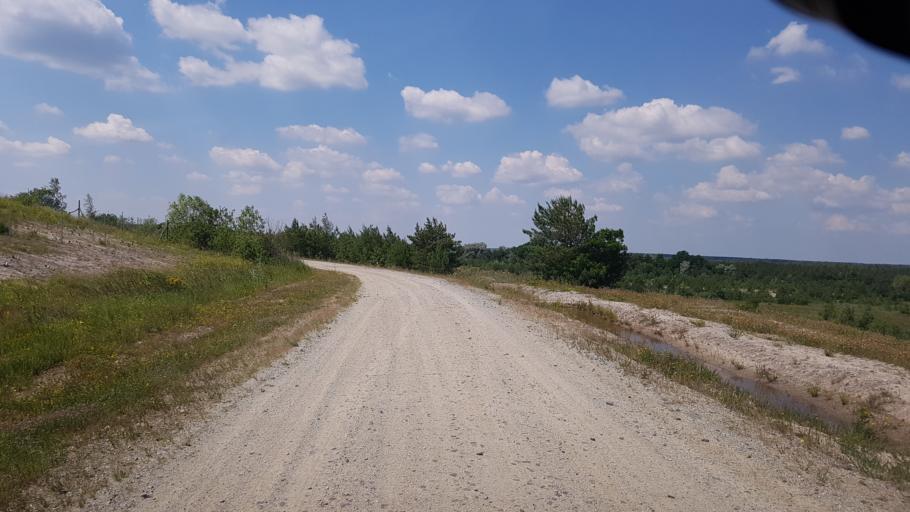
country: DE
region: Brandenburg
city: Sallgast
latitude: 51.5584
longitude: 13.7889
